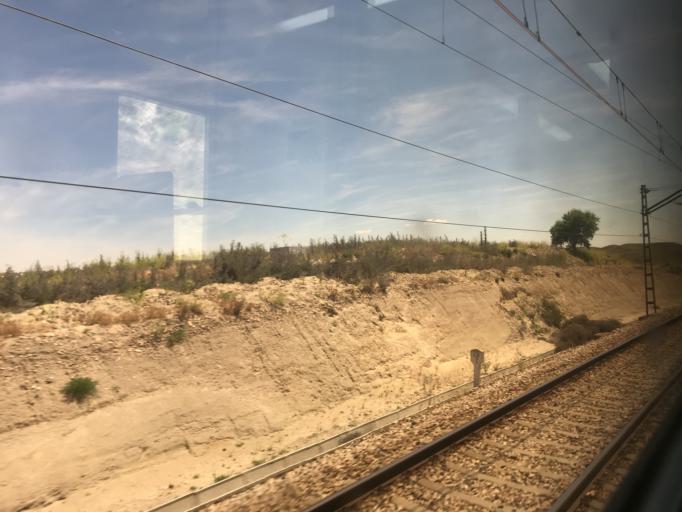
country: ES
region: Madrid
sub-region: Provincia de Madrid
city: Ciempozuelos
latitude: 40.1844
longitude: -3.6406
